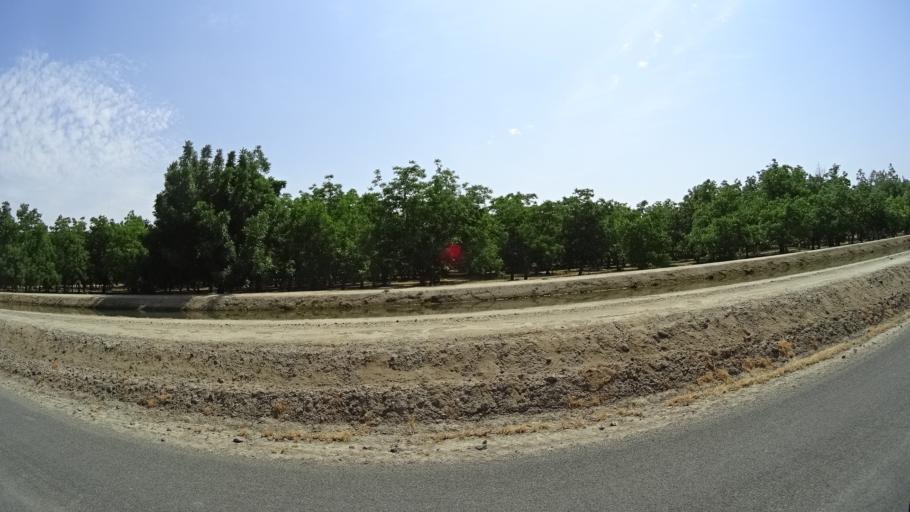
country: US
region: California
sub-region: Fresno County
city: Laton
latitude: 36.4004
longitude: -119.7624
